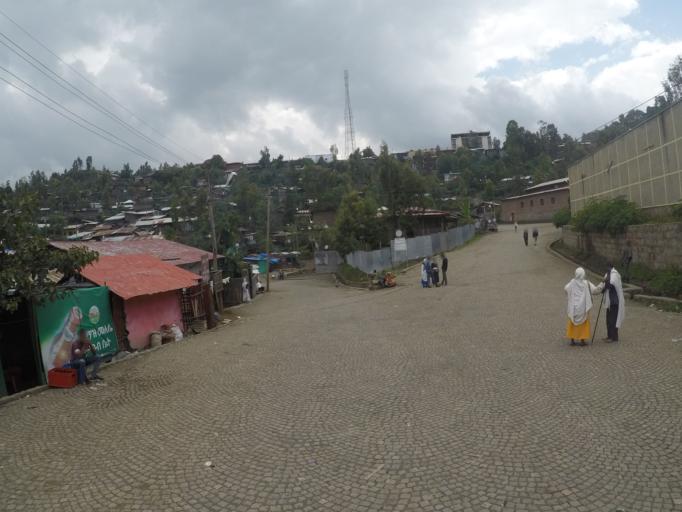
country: ET
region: Amhara
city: Lalibela
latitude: 12.0348
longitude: 39.0439
